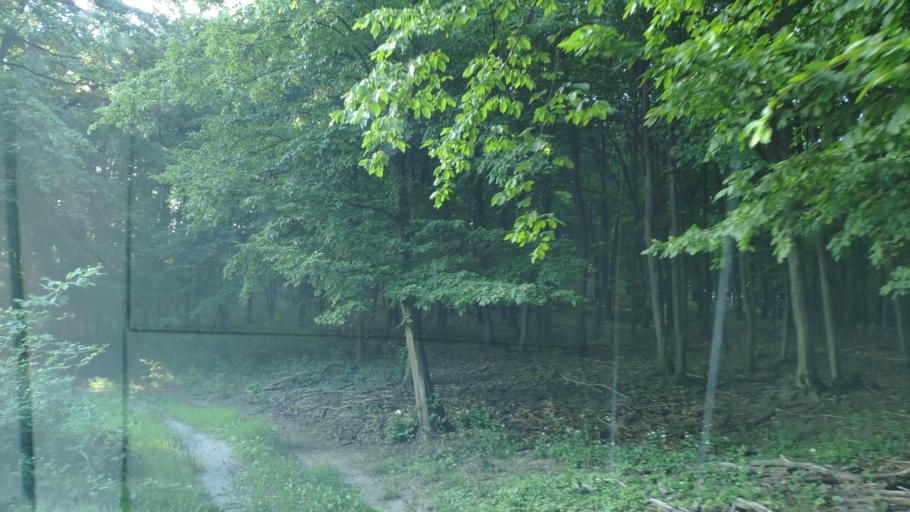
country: HU
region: Borsod-Abauj-Zemplen
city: Arlo
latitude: 48.2454
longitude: 20.1365
